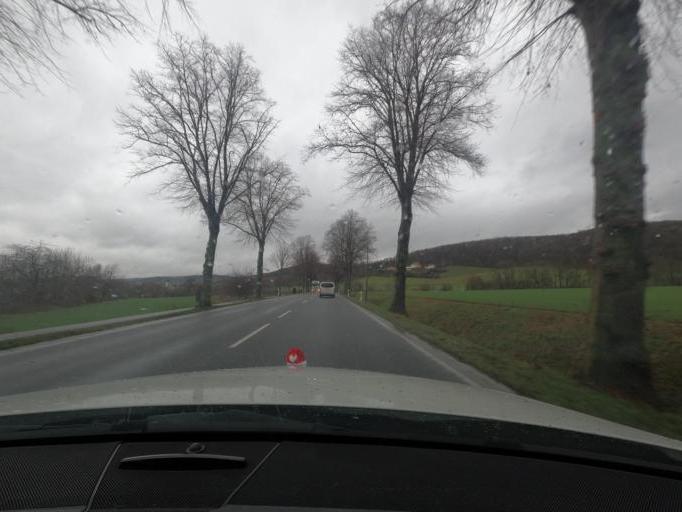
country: DE
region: Lower Saxony
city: Einbeck
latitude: 51.7887
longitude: 9.9324
